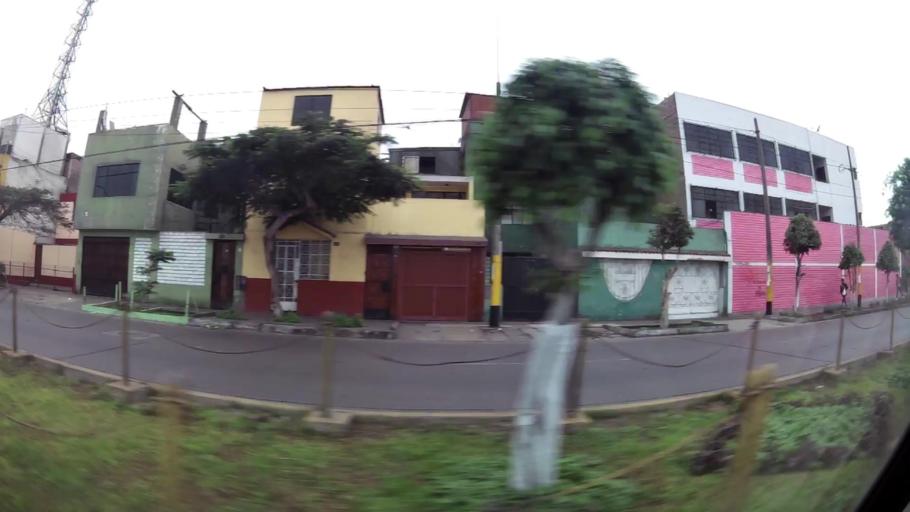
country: PE
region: Lima
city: Lima
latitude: -12.0613
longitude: -77.0529
